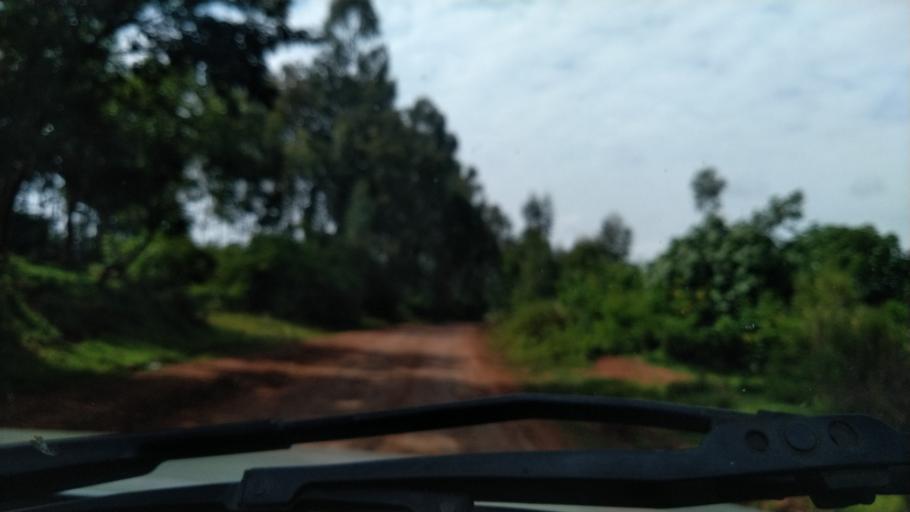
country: ET
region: Oromiya
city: Jima
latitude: 7.6529
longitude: 37.2490
